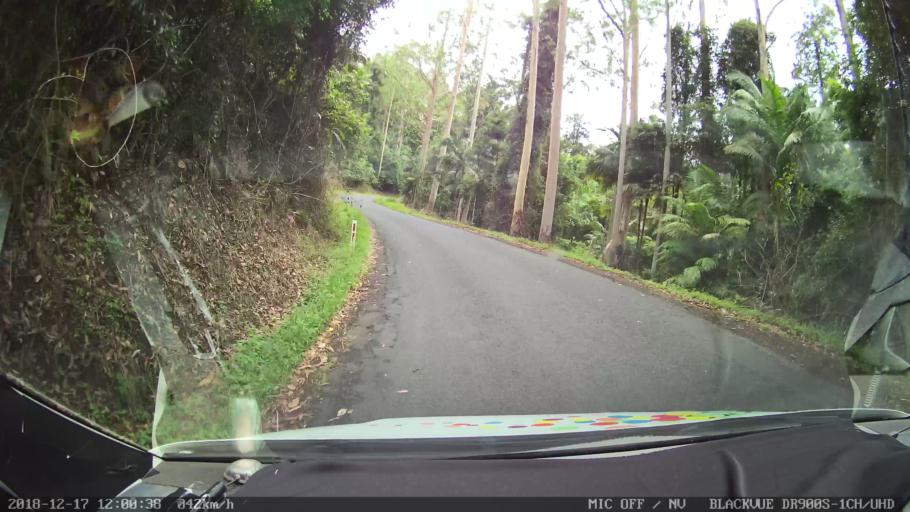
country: AU
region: New South Wales
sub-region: Kyogle
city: Kyogle
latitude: -28.5246
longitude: 152.5690
